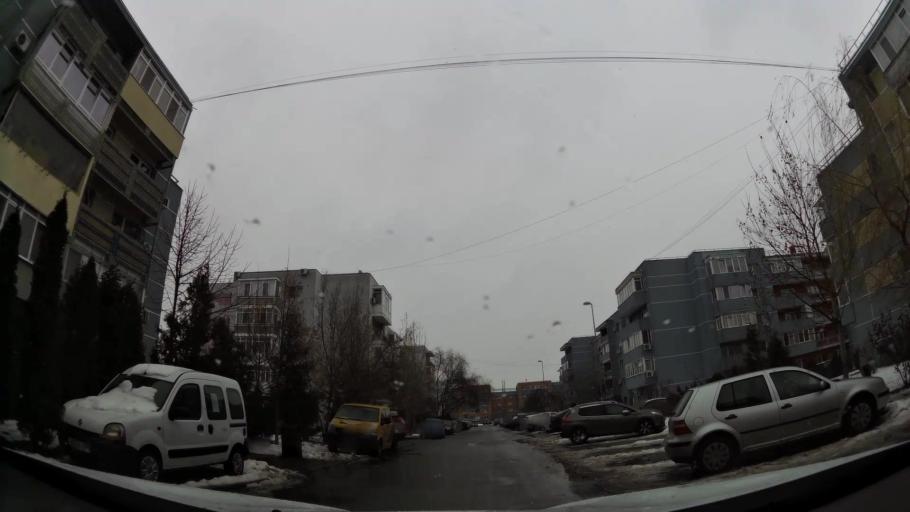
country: RO
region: Ilfov
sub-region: Comuna Chiajna
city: Rosu
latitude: 44.4202
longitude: 26.0046
